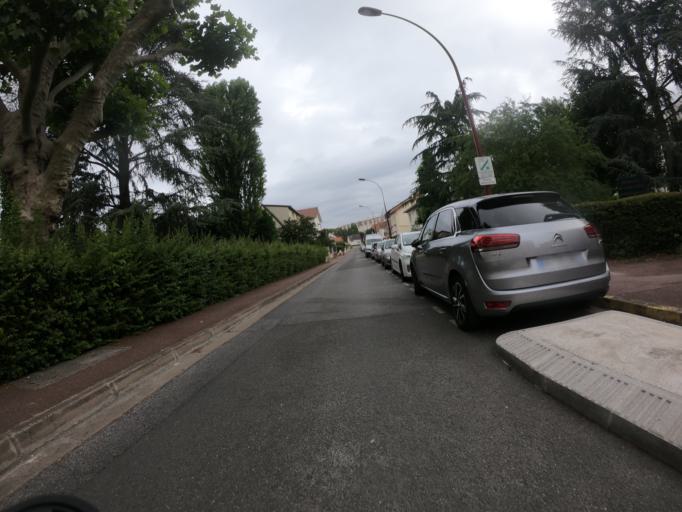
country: FR
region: Ile-de-France
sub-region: Departement du Val-de-Marne
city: Fresnes
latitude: 48.7541
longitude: 2.3112
